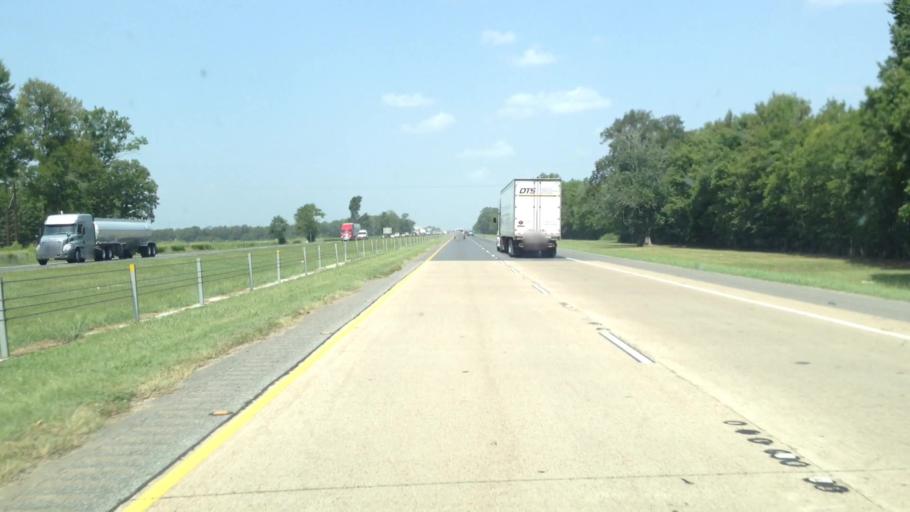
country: US
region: Louisiana
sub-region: Ouachita Parish
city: Lakeshore
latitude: 32.4900
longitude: -92.0013
